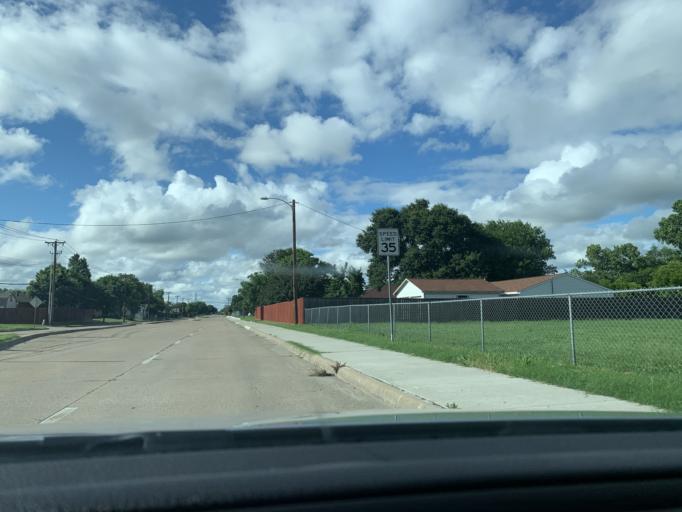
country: US
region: Texas
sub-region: Dallas County
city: Cedar Hill
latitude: 32.6478
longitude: -97.0278
